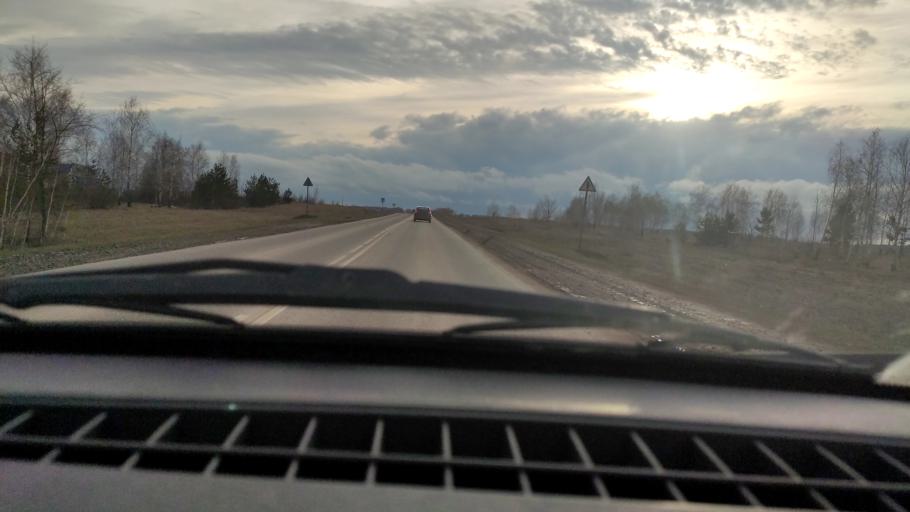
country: RU
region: Bashkortostan
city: Davlekanovo
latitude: 54.2376
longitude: 55.0442
